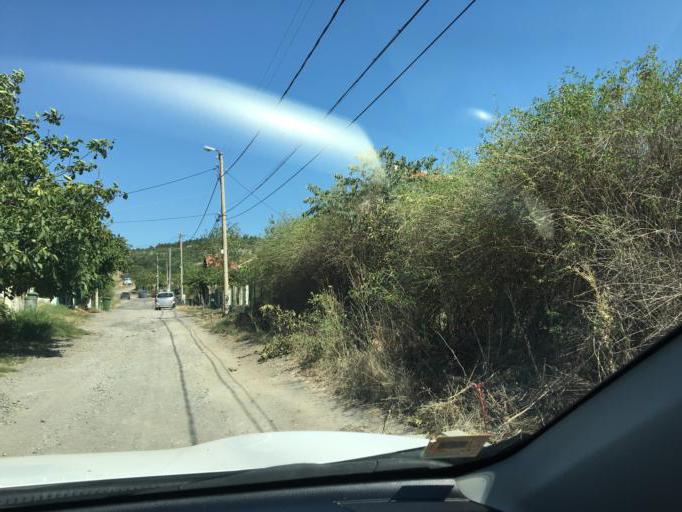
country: BG
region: Burgas
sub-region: Obshtina Kameno
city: Kameno
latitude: 42.6318
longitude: 27.3897
